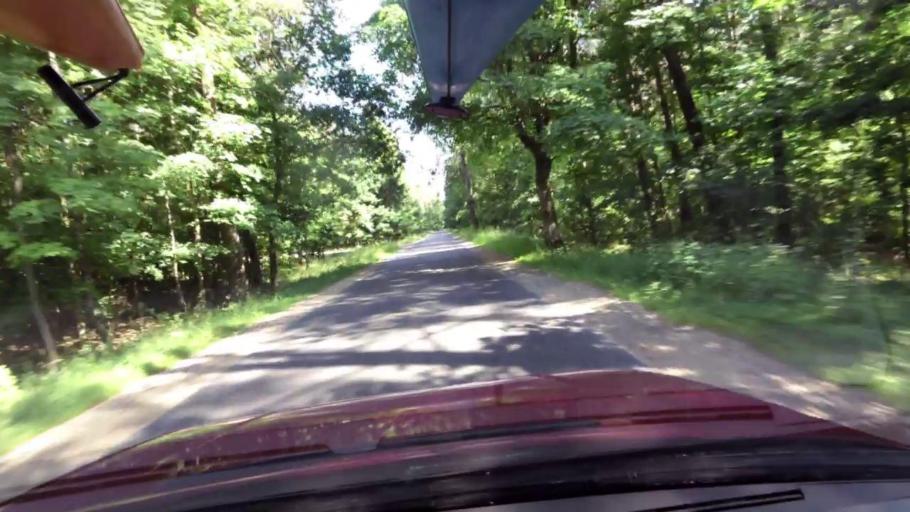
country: PL
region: Pomeranian Voivodeship
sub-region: Powiat slupski
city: Kepice
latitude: 54.1366
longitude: 16.9283
